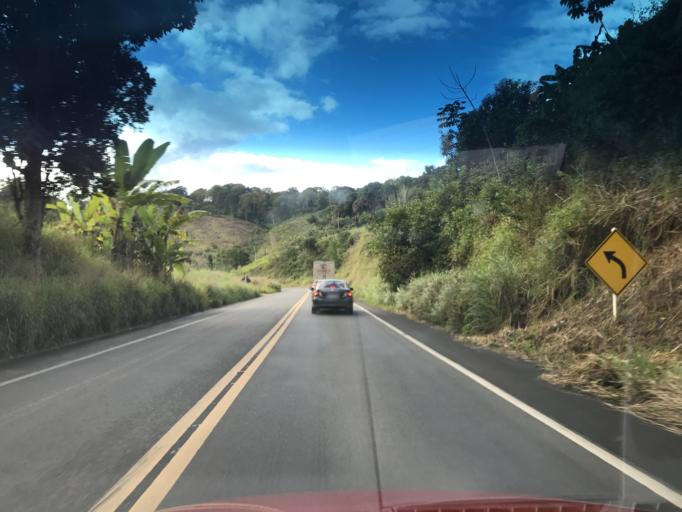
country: BR
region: Bahia
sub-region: Ibirapitanga
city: Ibirapitanga
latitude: -14.1739
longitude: -39.3235
